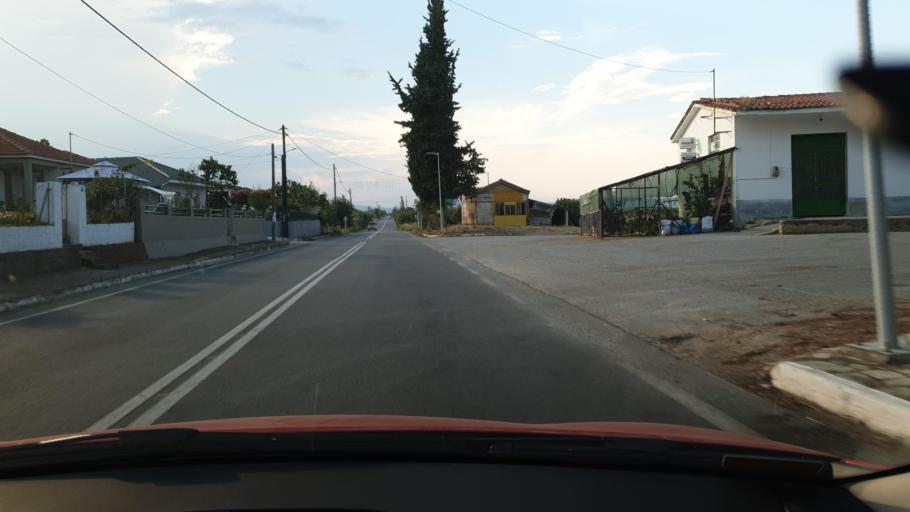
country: GR
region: Thessaly
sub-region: Nomos Magnisias
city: Almyros
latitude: 39.1632
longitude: 22.7929
